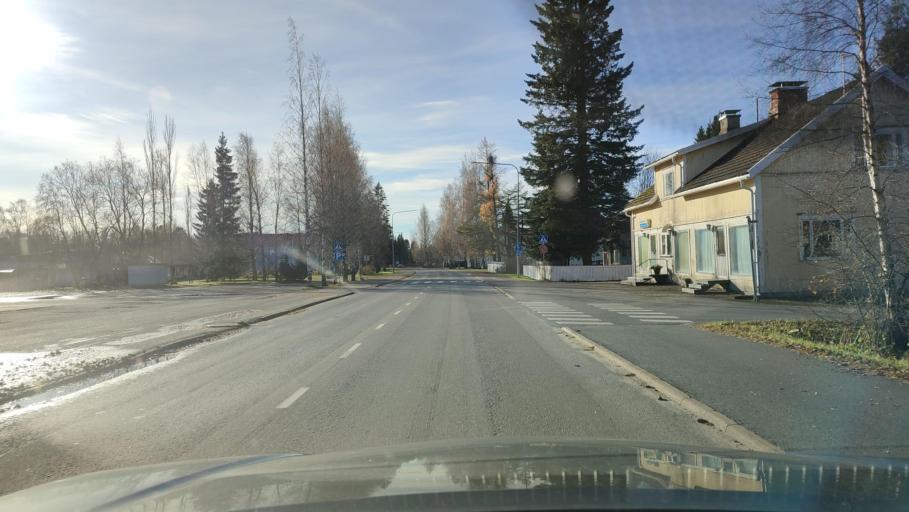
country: FI
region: Southern Ostrobothnia
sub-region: Suupohja
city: Teuva
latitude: 62.4841
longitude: 21.7450
